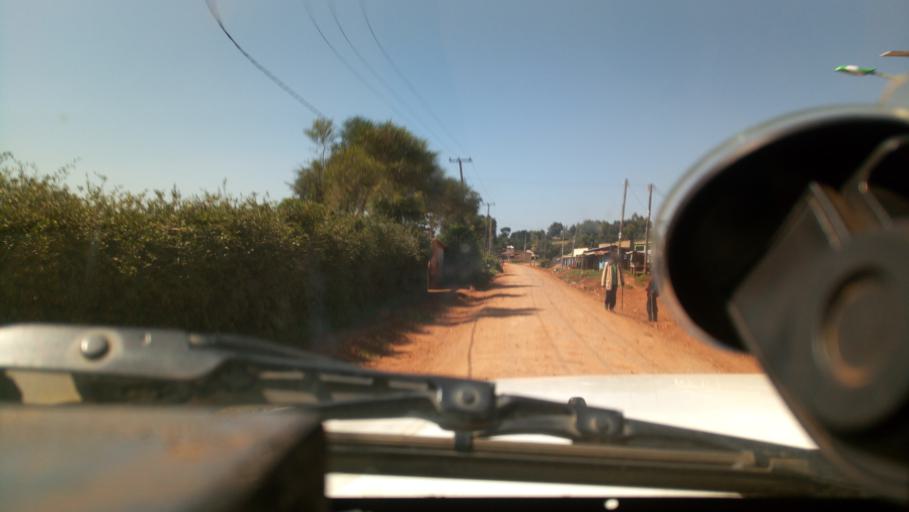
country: KE
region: Nyamira District
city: Nyamira
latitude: -0.5643
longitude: 34.9766
